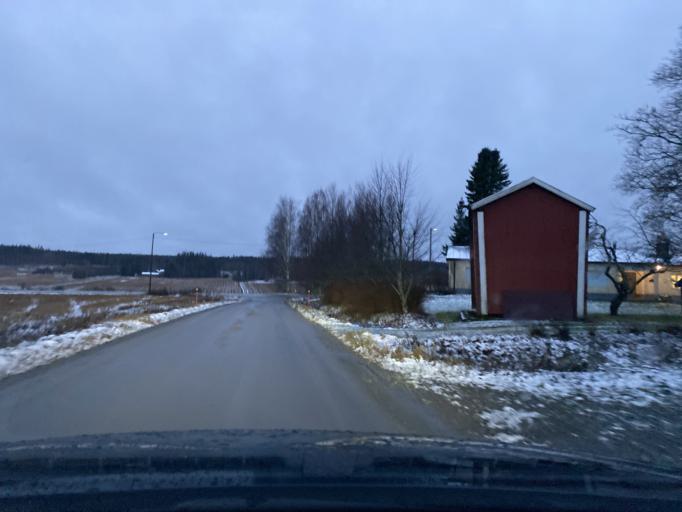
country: FI
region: Pirkanmaa
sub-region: Lounais-Pirkanmaa
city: Punkalaidun
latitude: 61.1393
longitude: 22.9630
